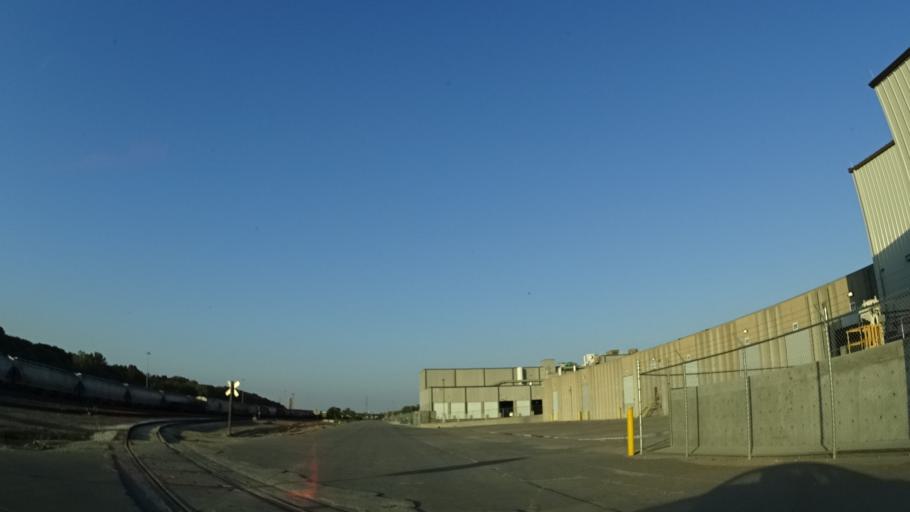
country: US
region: Nebraska
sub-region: Douglas County
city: Omaha
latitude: 41.2194
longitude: -95.9255
